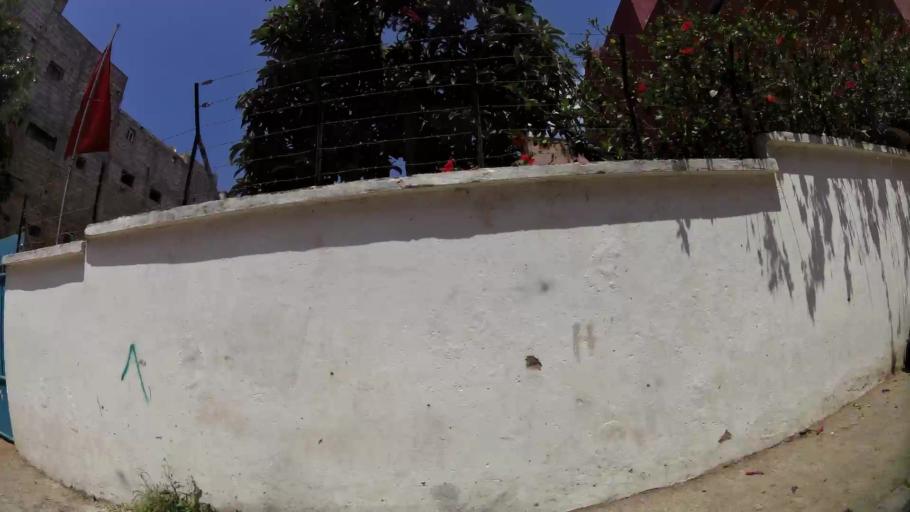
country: MA
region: Rabat-Sale-Zemmour-Zaer
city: Sale
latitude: 34.0621
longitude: -6.7919
